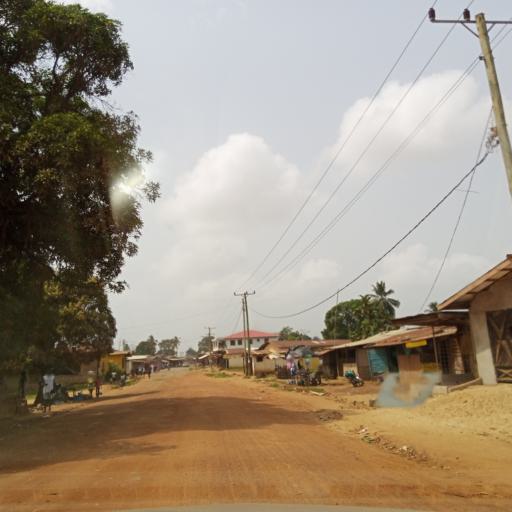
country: LR
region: Montserrado
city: Monrovia
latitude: 6.3485
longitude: -10.7311
